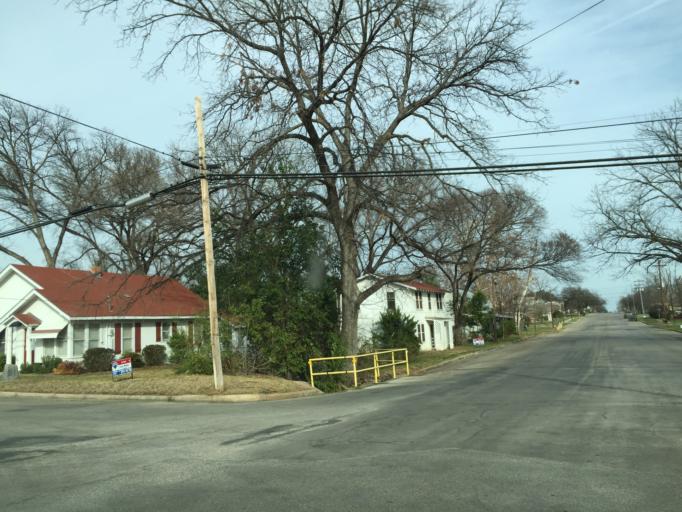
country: US
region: Texas
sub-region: Llano County
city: Llano
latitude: 30.7493
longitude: -98.6749
